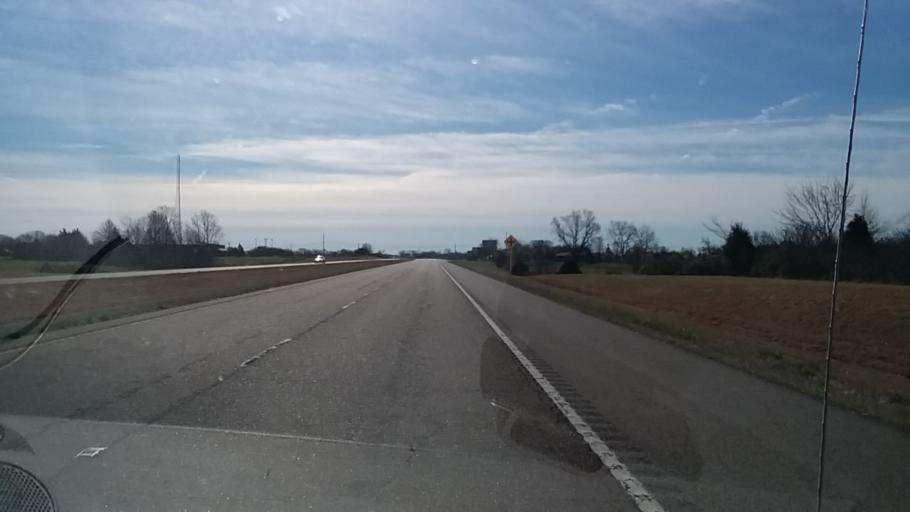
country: US
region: Tennessee
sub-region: Crockett County
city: Alamo
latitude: 35.7850
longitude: -89.1473
